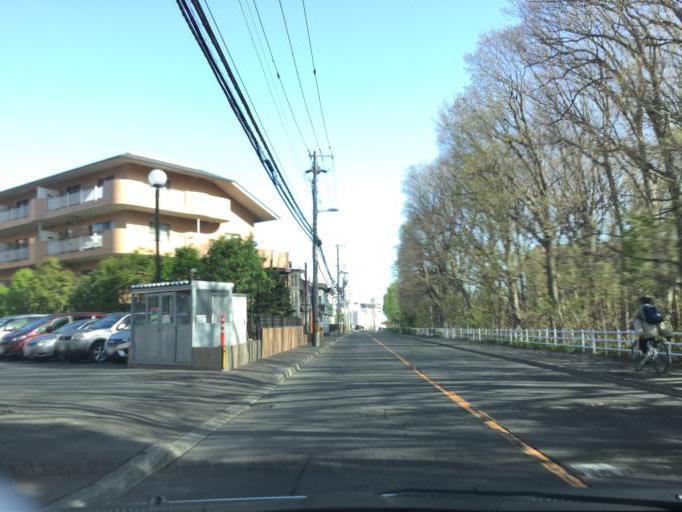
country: JP
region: Hokkaido
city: Sapporo
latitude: 43.0217
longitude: 141.4473
